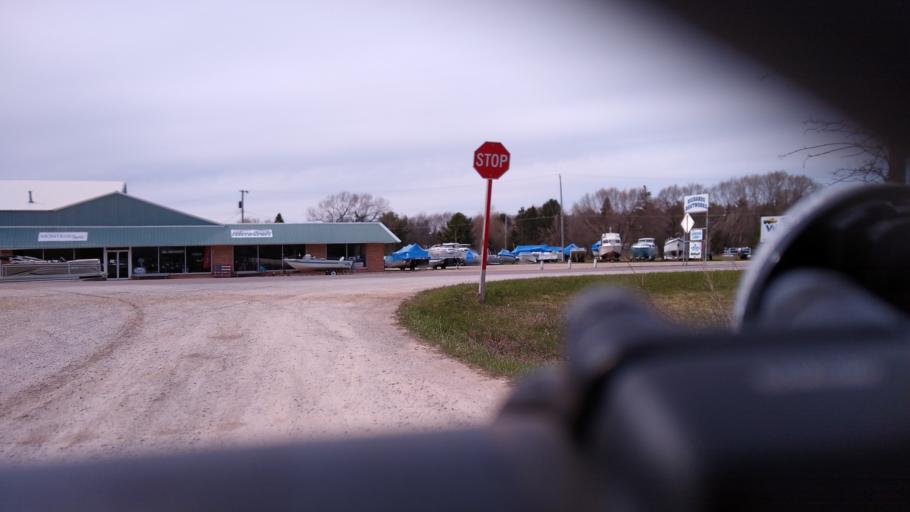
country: US
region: Michigan
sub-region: Delta County
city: Escanaba
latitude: 45.6787
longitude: -87.1403
